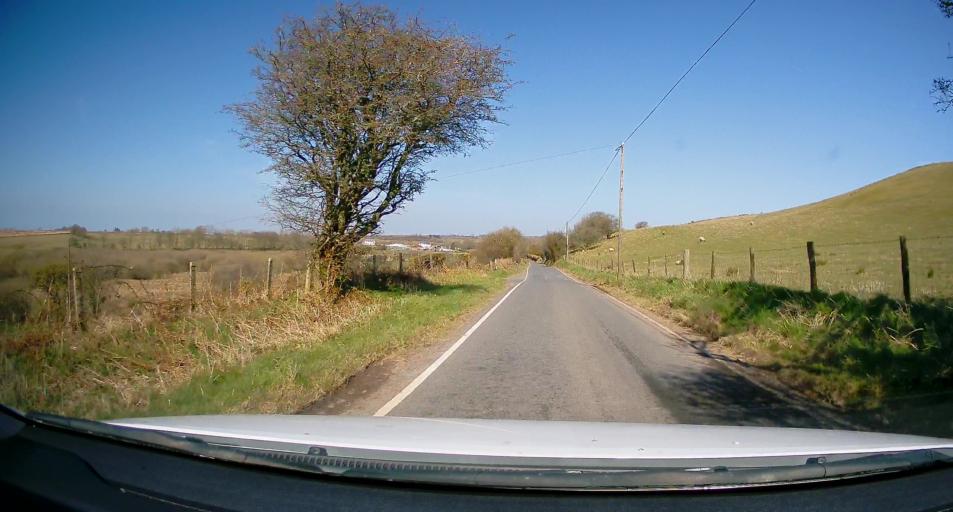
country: GB
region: Wales
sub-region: County of Ceredigion
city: Lledrod
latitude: 52.2780
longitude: -4.0636
